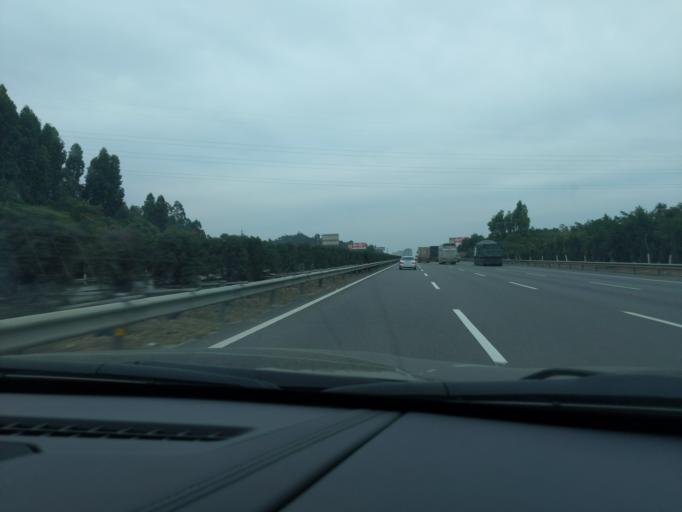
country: CN
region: Fujian
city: Anhai
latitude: 24.7146
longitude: 118.3979
